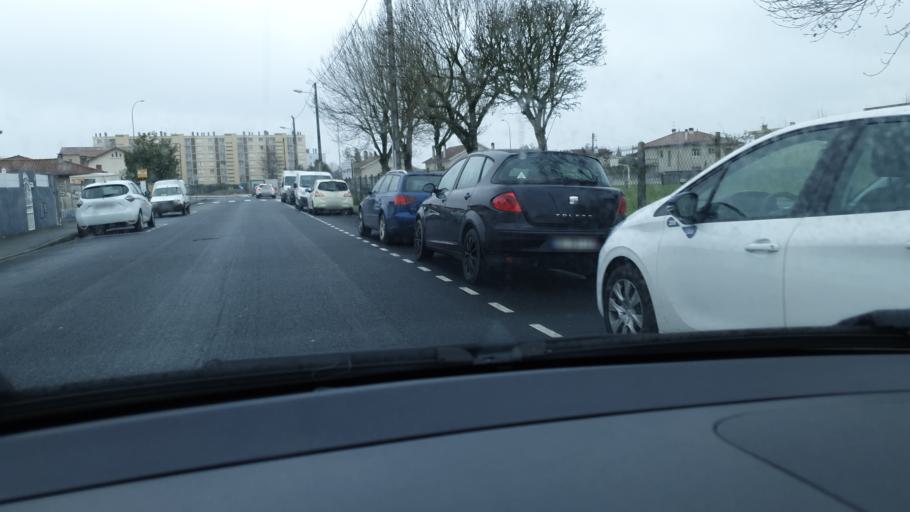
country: FR
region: Midi-Pyrenees
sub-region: Departement des Hautes-Pyrenees
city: Tarbes
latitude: 43.2411
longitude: 0.0533
